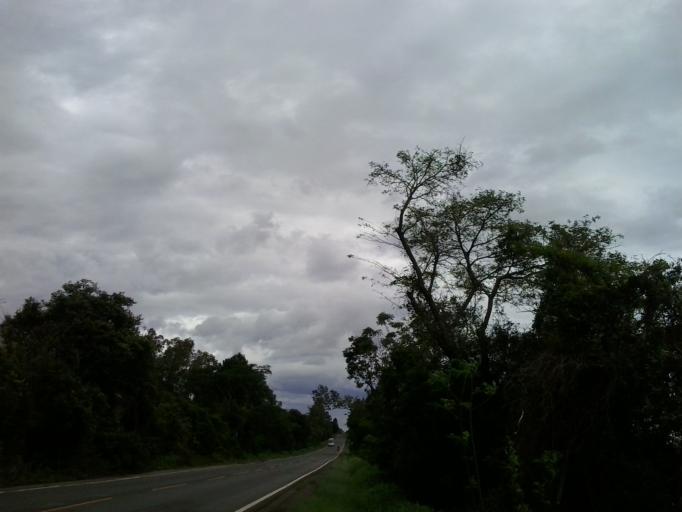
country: BR
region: Rio Grande do Sul
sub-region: Santa Maria
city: Santa Maria
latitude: -29.7316
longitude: -53.5503
